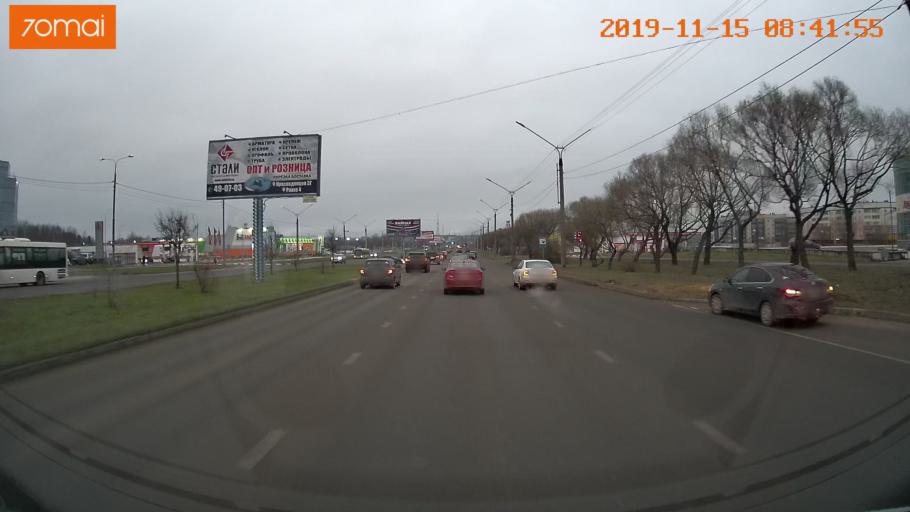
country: RU
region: Vologda
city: Cherepovets
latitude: 59.0990
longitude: 37.9106
